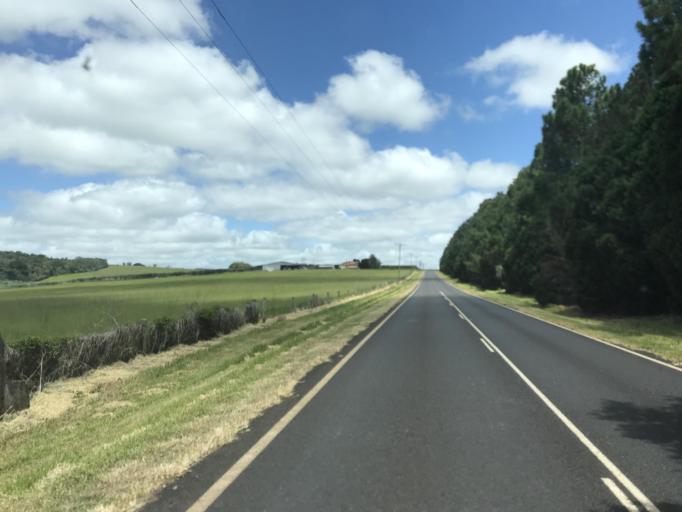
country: AU
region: Queensland
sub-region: Tablelands
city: Ravenshoe
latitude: -17.5079
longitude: 145.4630
